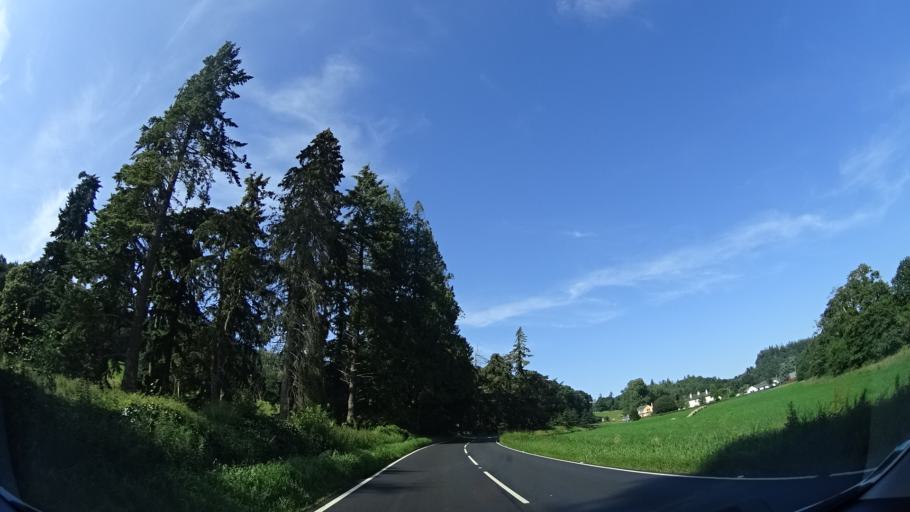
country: GB
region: Scotland
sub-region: Highland
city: Inverness
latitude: 57.4310
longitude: -4.3084
